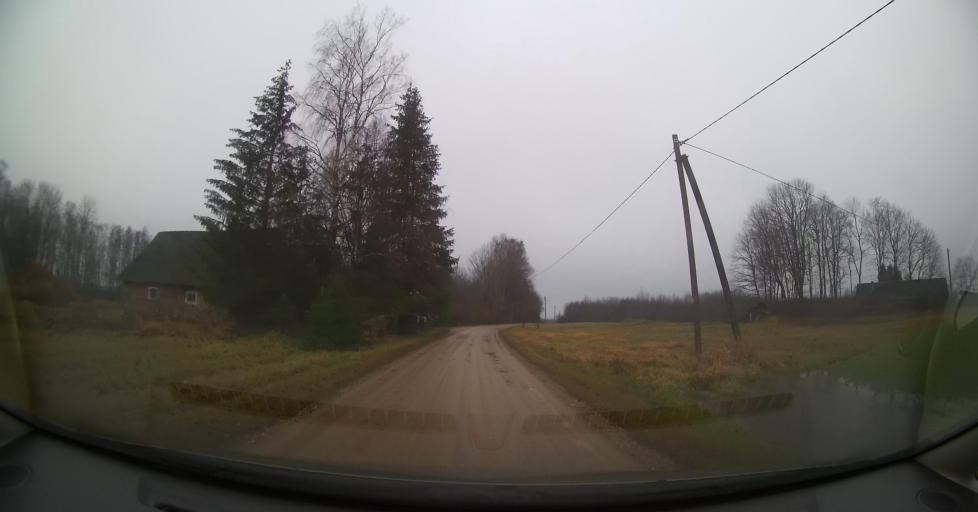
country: EE
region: Tartu
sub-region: Tartu linn
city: Tartu
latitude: 58.3912
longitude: 27.0039
